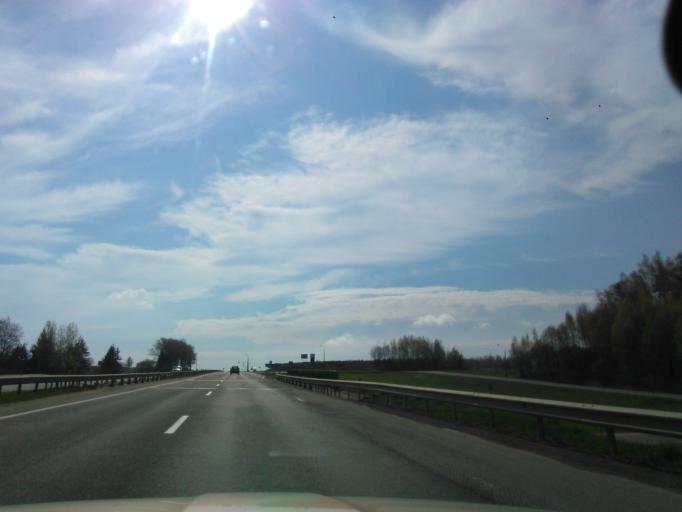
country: BY
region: Minsk
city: Novosel'ye
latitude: 53.9255
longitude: 27.1638
